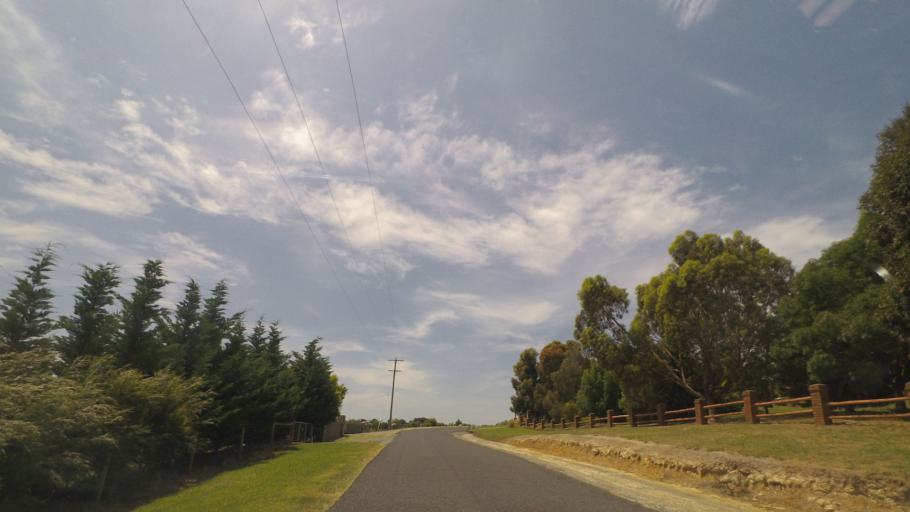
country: AU
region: Victoria
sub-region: Yarra Ranges
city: Chirnside Park
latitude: -37.7526
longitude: 145.3007
